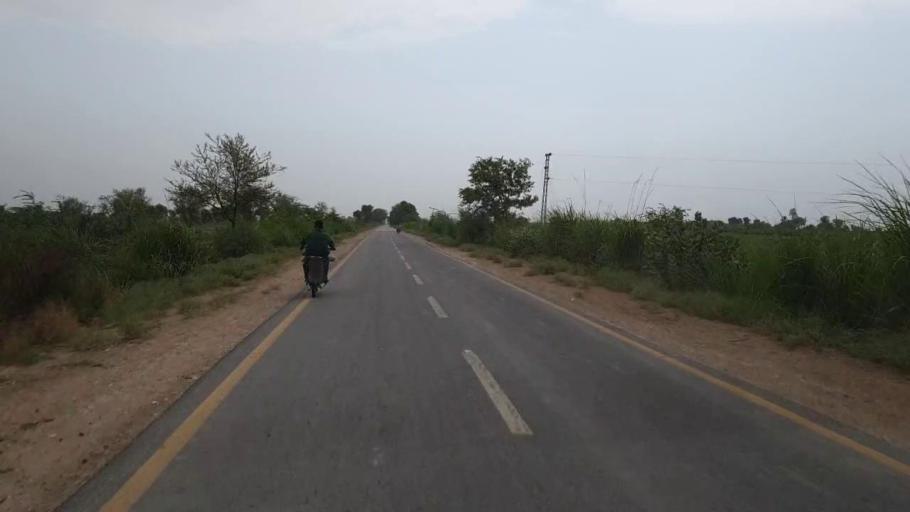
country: PK
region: Sindh
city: Bandhi
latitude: 26.5893
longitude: 68.2148
